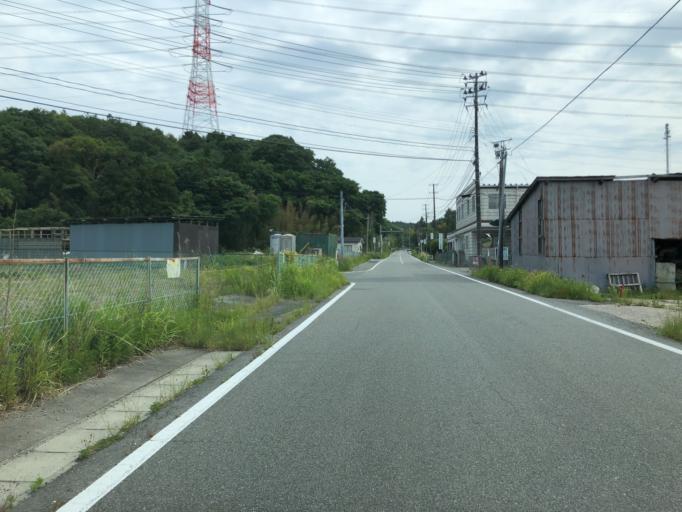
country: JP
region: Fukushima
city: Namie
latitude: 37.3178
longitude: 141.0079
